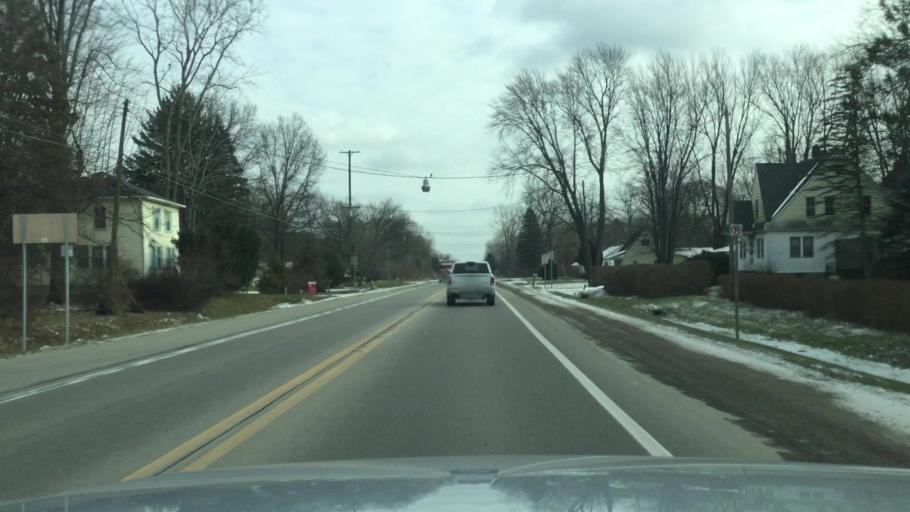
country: US
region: Michigan
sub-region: Saginaw County
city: Birch Run
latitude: 43.1772
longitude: -83.8113
